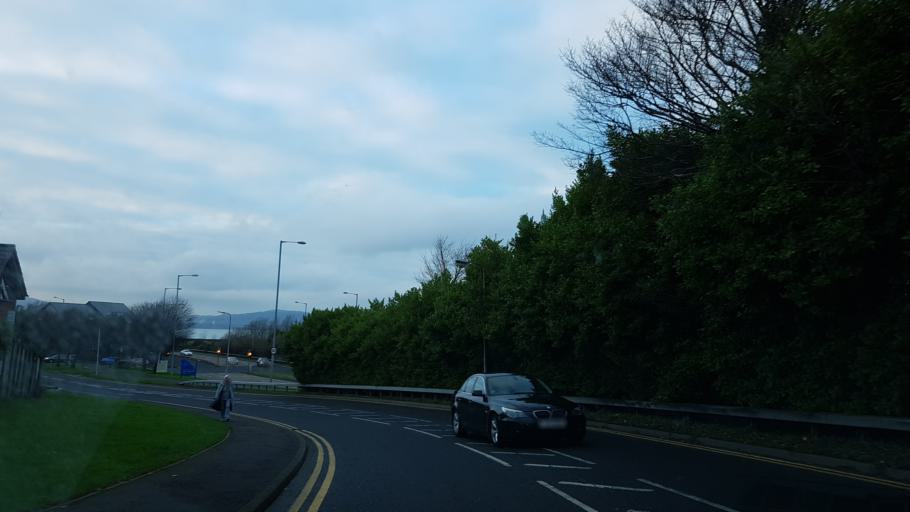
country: GB
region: Northern Ireland
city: Holywood
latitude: 54.6442
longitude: -5.8245
